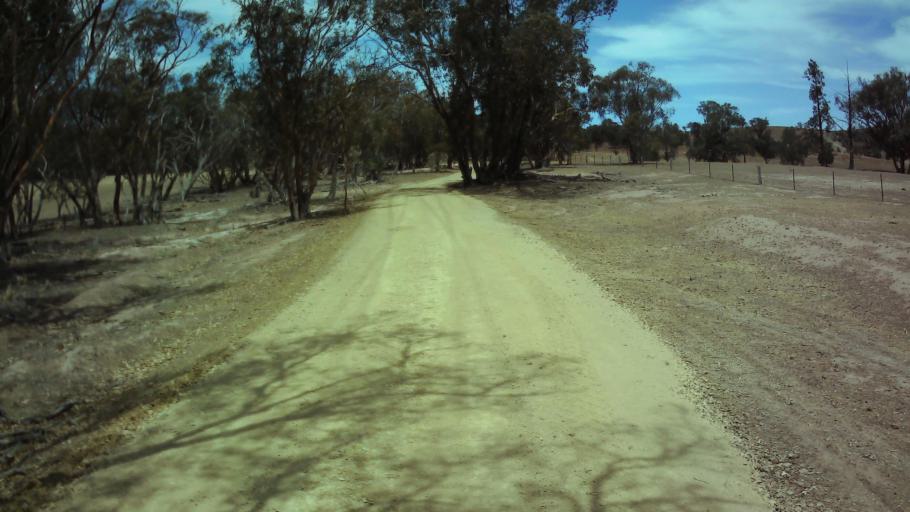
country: AU
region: New South Wales
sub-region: Weddin
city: Grenfell
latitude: -33.7842
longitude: 148.1518
